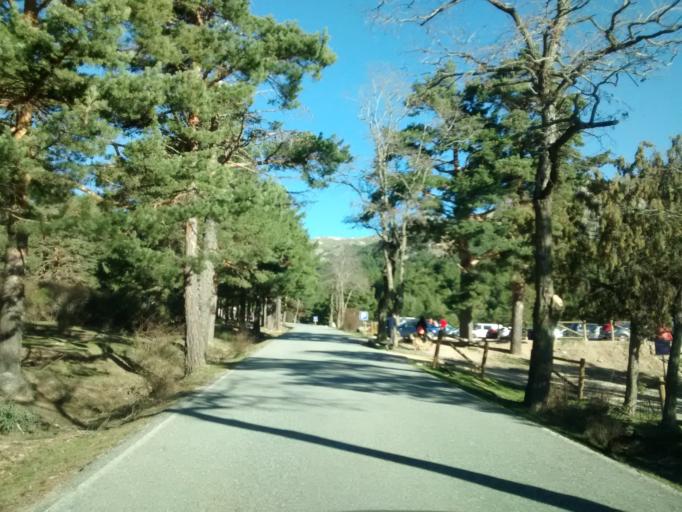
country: ES
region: Madrid
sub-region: Provincia de Madrid
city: Navacerrada
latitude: 40.7516
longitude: -3.9932
